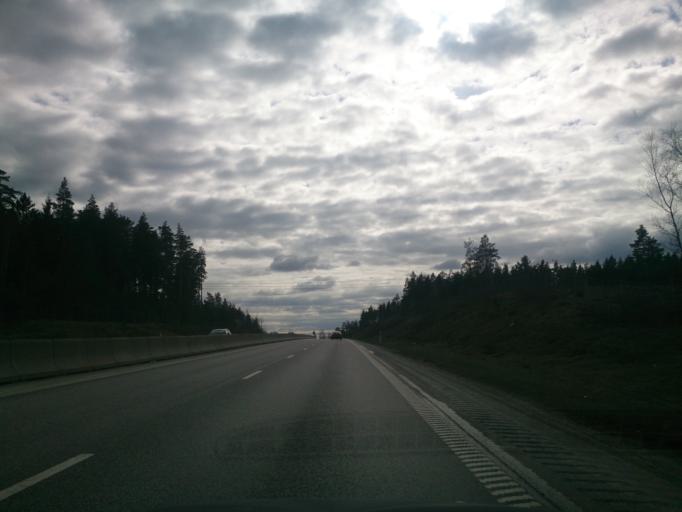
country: SE
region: OEstergoetland
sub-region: Norrkopings Kommun
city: Kimstad
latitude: 58.5171
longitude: 15.9978
